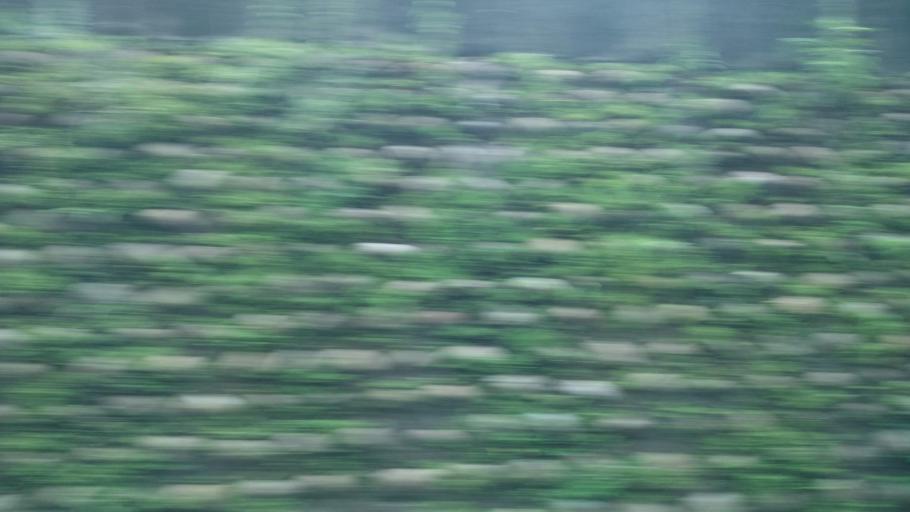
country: TW
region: Taiwan
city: Daxi
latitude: 24.9119
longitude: 121.3898
